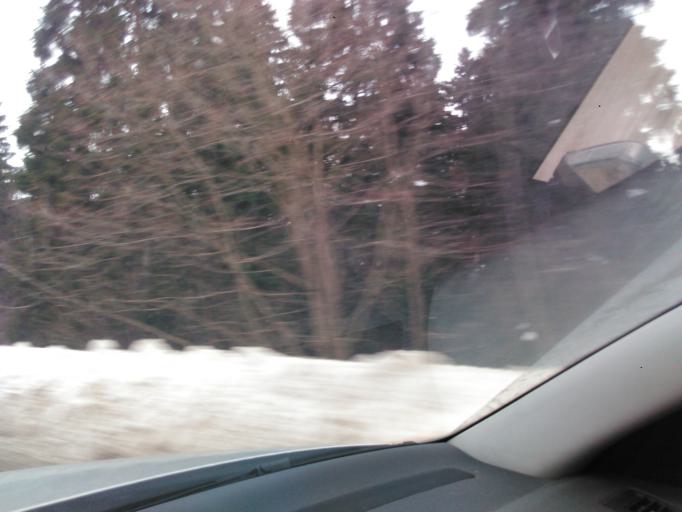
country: RU
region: Moskovskaya
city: Dedenevo
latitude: 56.2644
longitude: 37.5683
